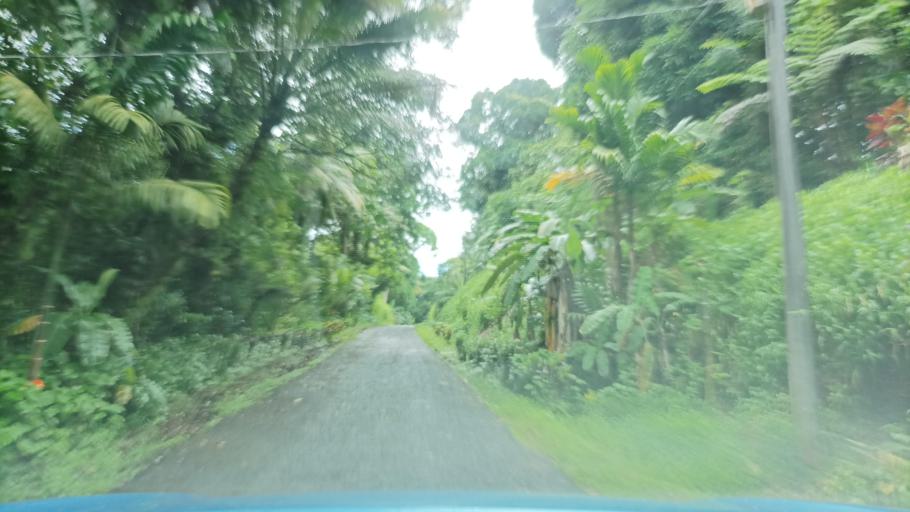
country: FM
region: Pohnpei
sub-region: Sokehs Municipality
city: Palikir - National Government Center
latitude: 6.8279
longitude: 158.1704
